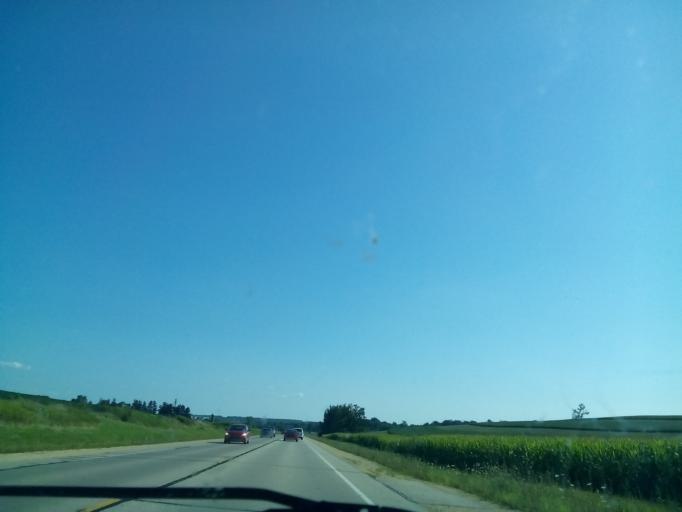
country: US
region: Wisconsin
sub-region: Green County
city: New Glarus
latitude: 42.8327
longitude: -89.6350
